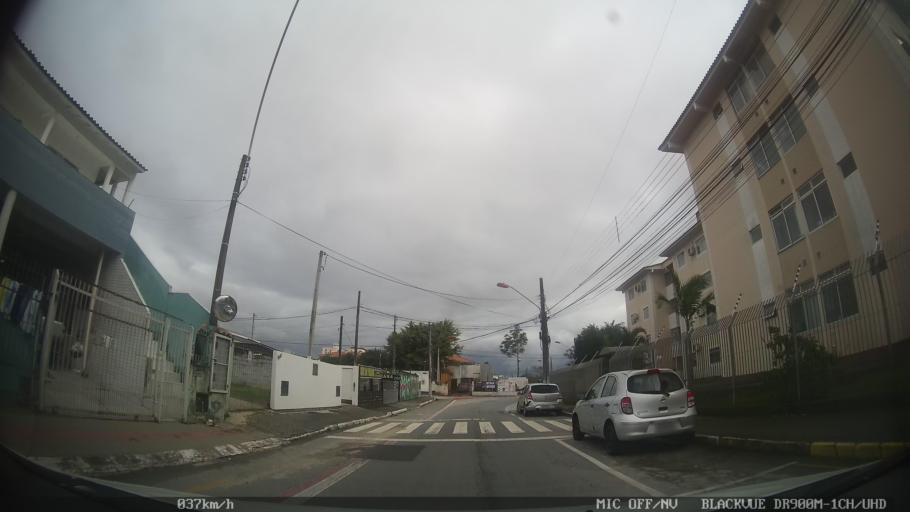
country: BR
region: Santa Catarina
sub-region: Sao Jose
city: Campinas
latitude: -27.5598
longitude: -48.6322
